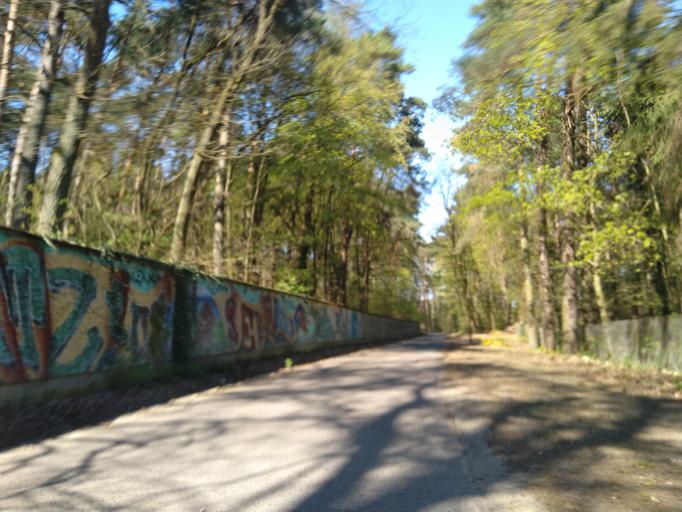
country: DE
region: Brandenburg
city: Biesenthal
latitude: 52.7709
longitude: 13.6042
